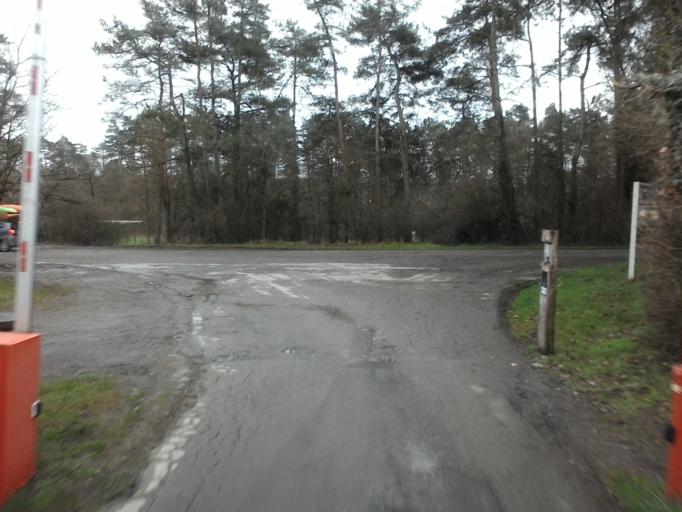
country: BE
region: Wallonia
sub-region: Province du Luxembourg
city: Wellin
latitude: 50.1113
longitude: 5.1336
